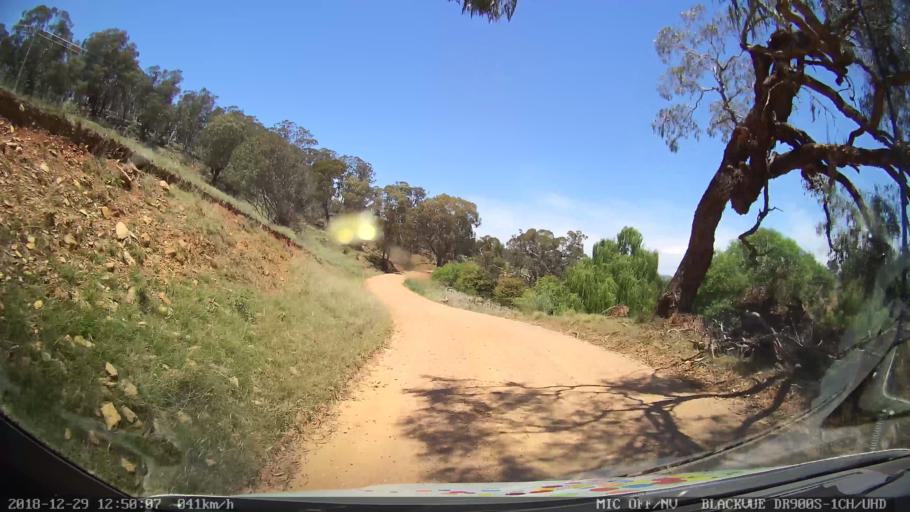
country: AU
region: Australian Capital Territory
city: Macarthur
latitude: -35.6683
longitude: 149.2041
